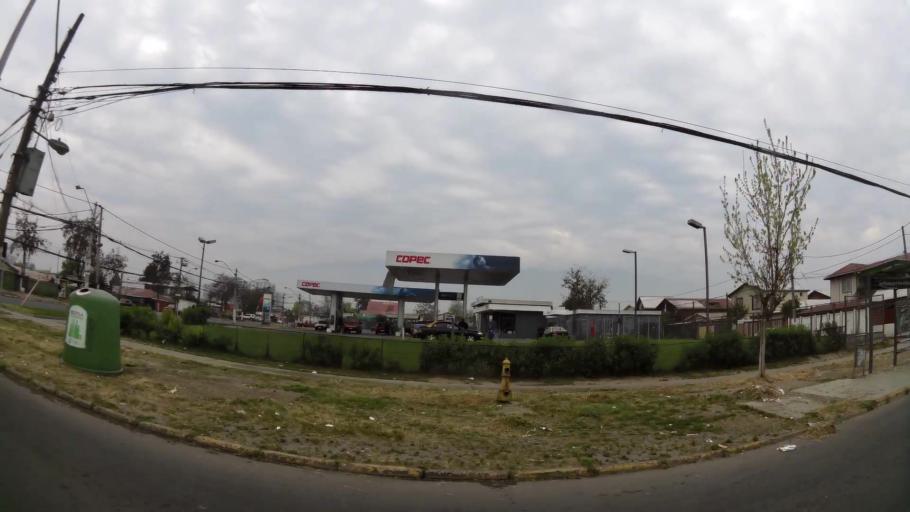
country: CL
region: Santiago Metropolitan
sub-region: Provincia de Santiago
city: Villa Presidente Frei, Nunoa, Santiago, Chile
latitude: -33.4909
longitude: -70.6065
